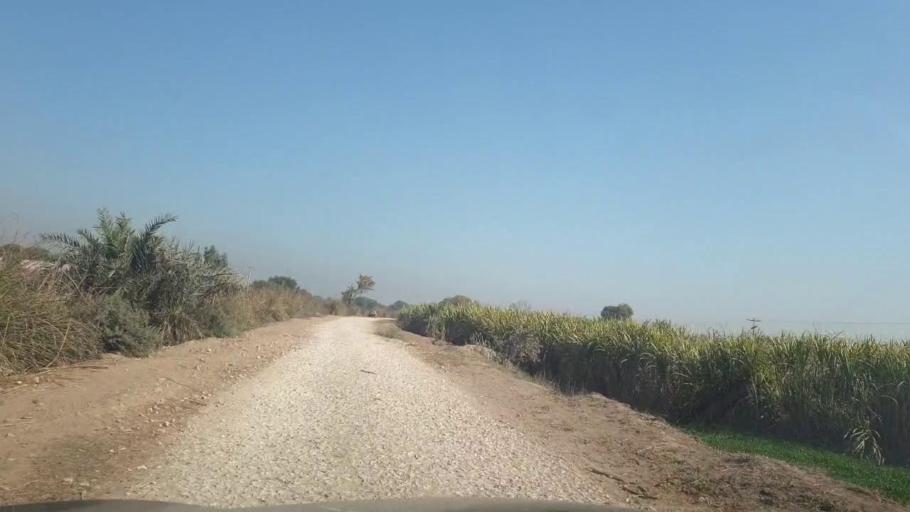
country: PK
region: Sindh
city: Mirpur Mathelo
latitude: 28.1267
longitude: 69.4965
